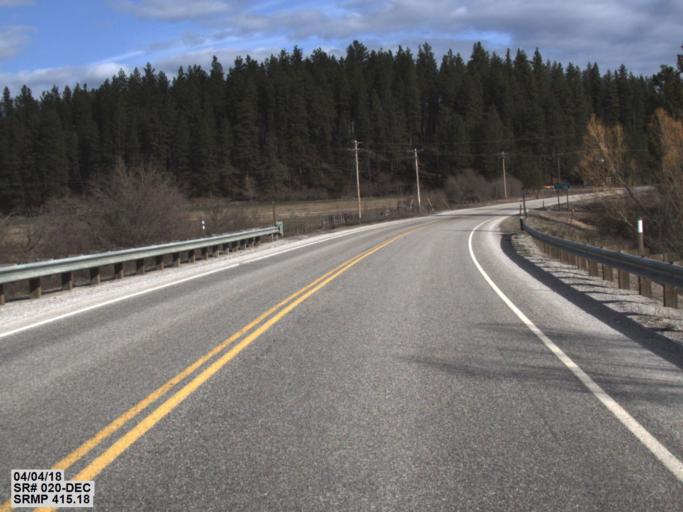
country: US
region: Washington
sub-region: Pend Oreille County
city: Newport
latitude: 48.3919
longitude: -117.3146
